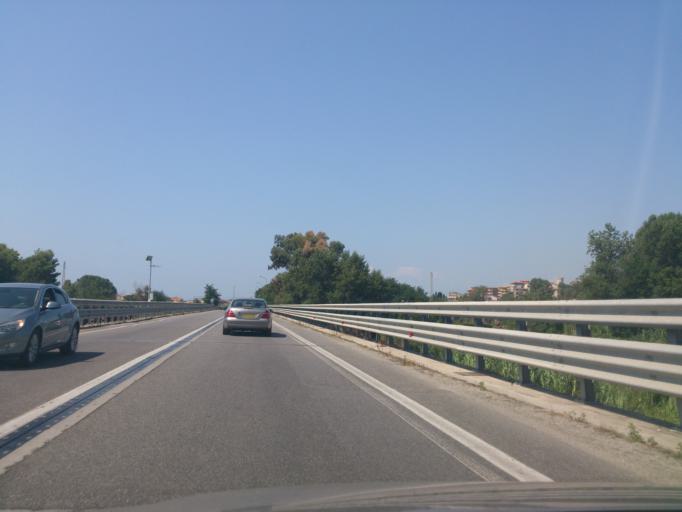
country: IT
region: Calabria
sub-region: Provincia di Reggio Calabria
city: Caulonia Marina
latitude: 38.3484
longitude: 16.4734
